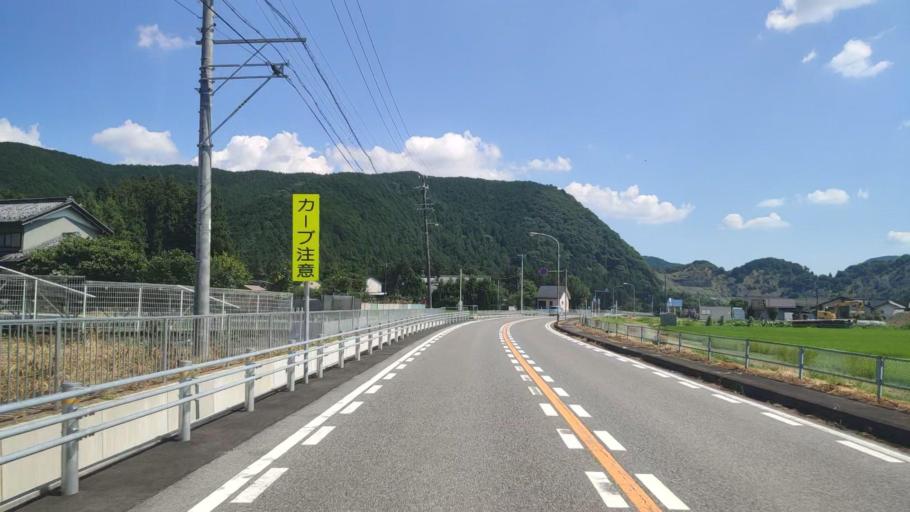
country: JP
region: Gifu
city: Godo
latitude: 35.5356
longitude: 136.6507
